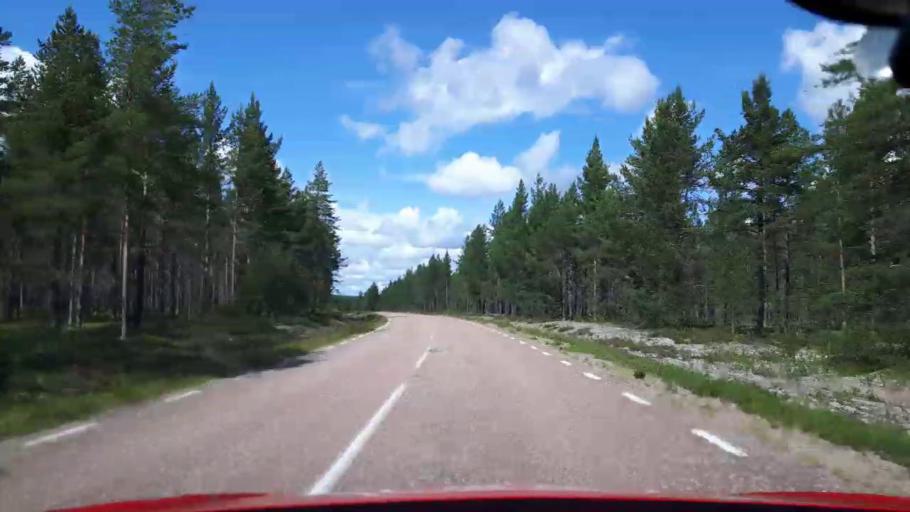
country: SE
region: Dalarna
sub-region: Alvdalens Kommun
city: AElvdalen
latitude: 61.8188
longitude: 13.5808
